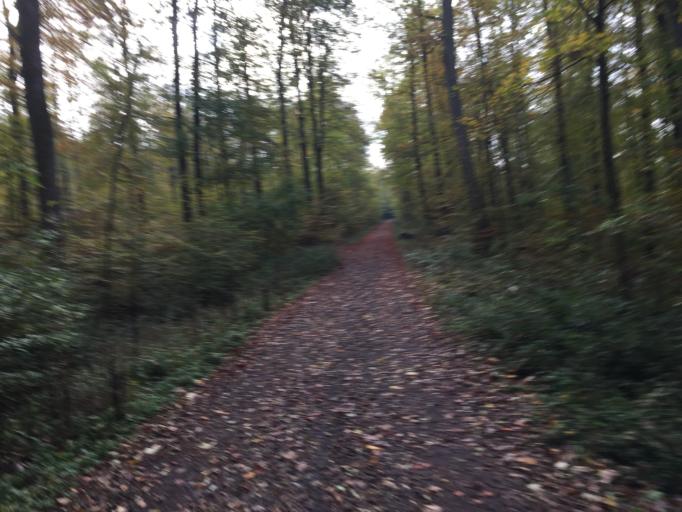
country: DE
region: Hesse
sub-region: Regierungsbezirk Giessen
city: Grunberg
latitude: 50.5845
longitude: 8.9894
